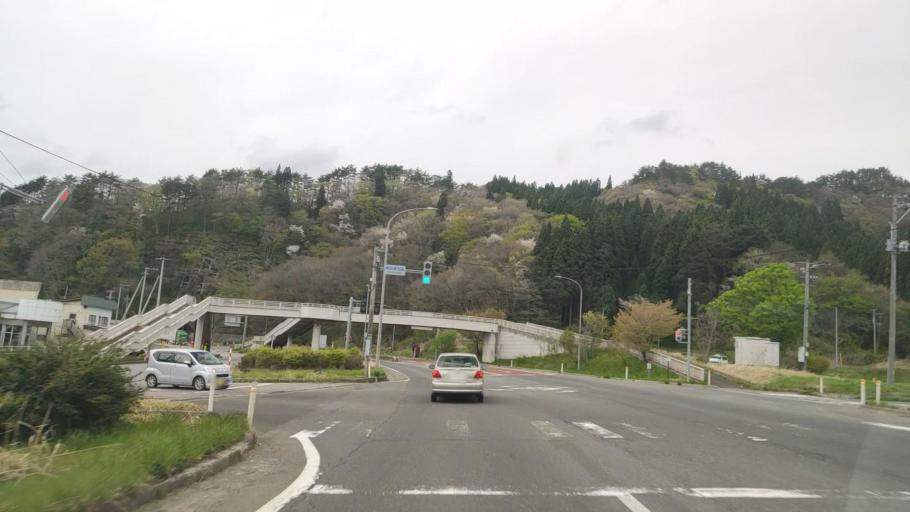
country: JP
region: Akita
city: Takanosu
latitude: 40.2174
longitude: 140.2604
